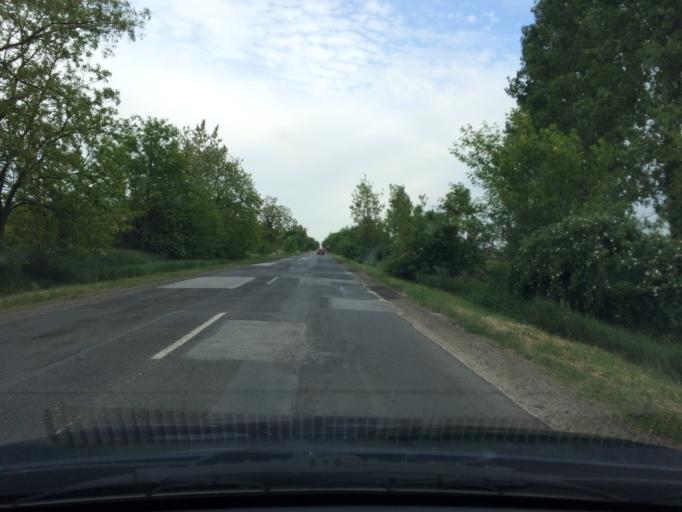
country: HU
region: Szabolcs-Szatmar-Bereg
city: Tiszavasvari
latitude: 47.9181
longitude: 21.3955
